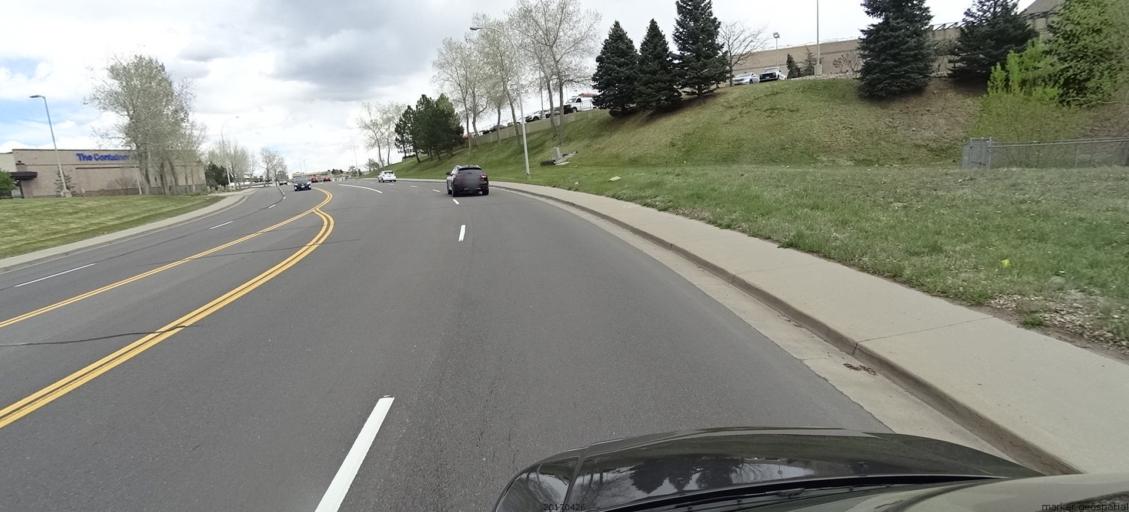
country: US
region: Colorado
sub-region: Adams County
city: Lone Tree
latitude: 39.5585
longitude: -104.8789
